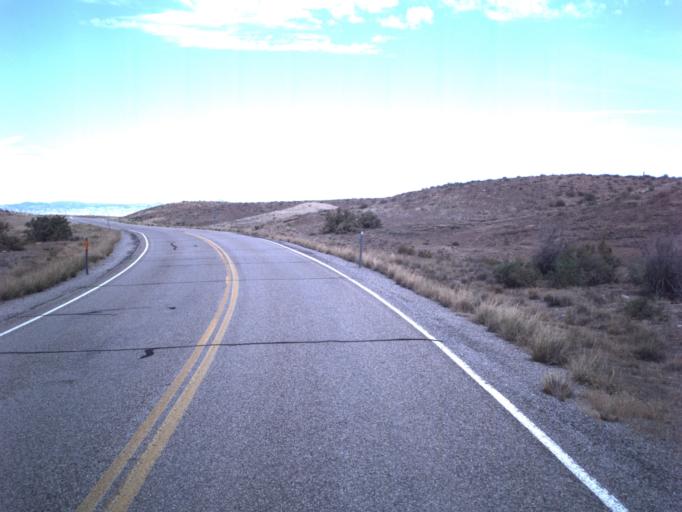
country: US
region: Utah
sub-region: Grand County
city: Moab
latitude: 38.9409
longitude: -109.3500
